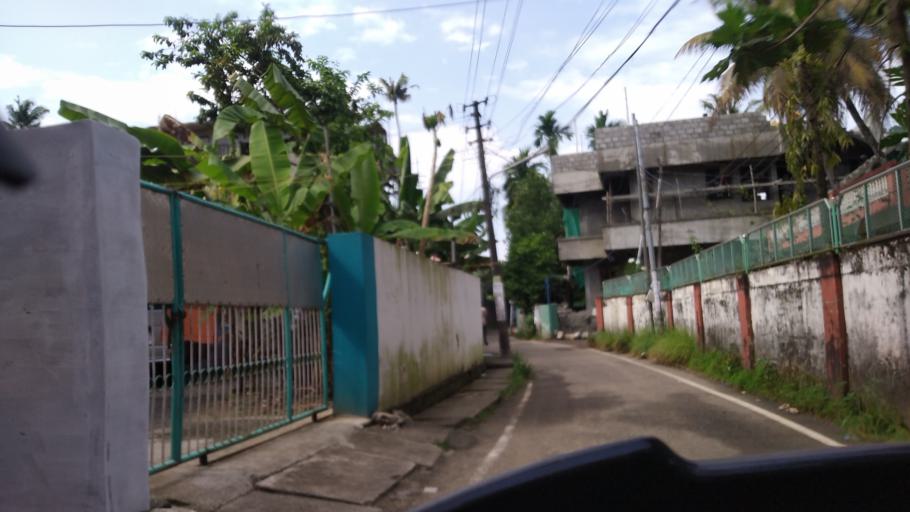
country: IN
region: Kerala
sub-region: Ernakulam
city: Cochin
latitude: 9.9854
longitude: 76.2999
